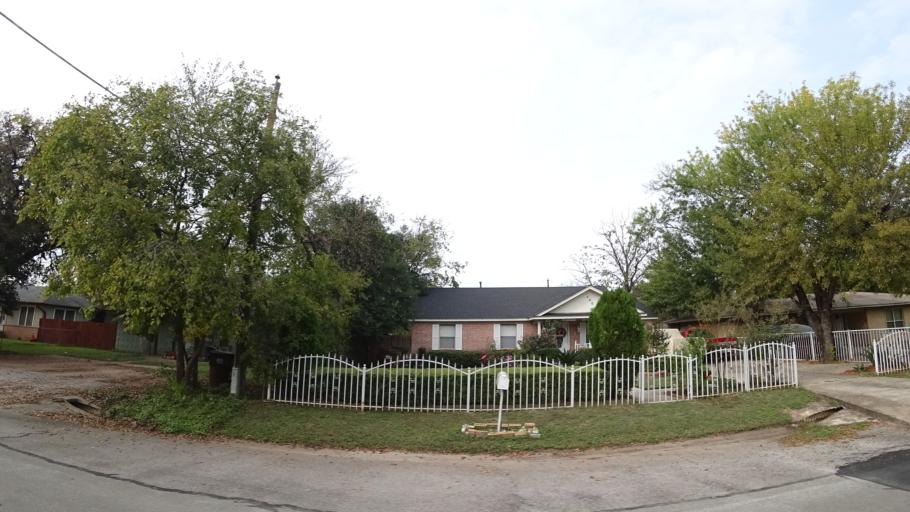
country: US
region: Texas
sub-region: Williamson County
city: Round Rock
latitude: 30.5124
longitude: -97.6648
